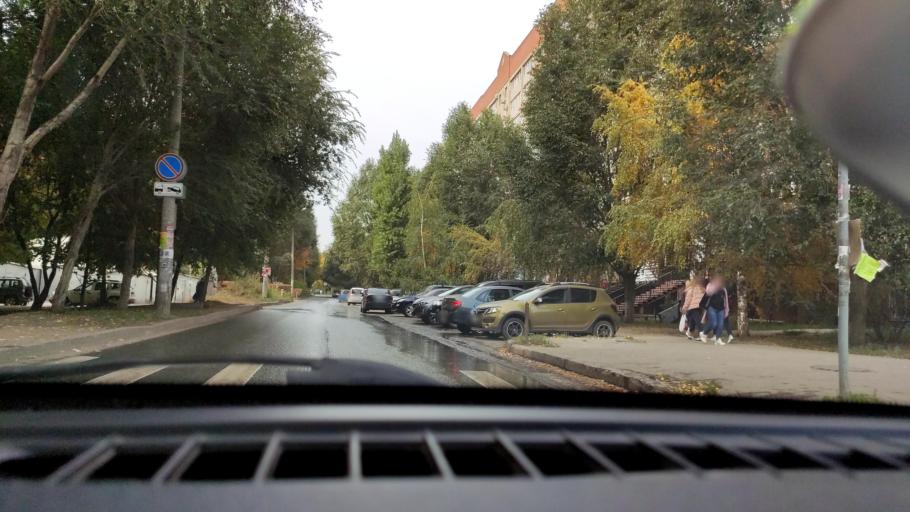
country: RU
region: Samara
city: Samara
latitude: 53.2310
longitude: 50.2516
